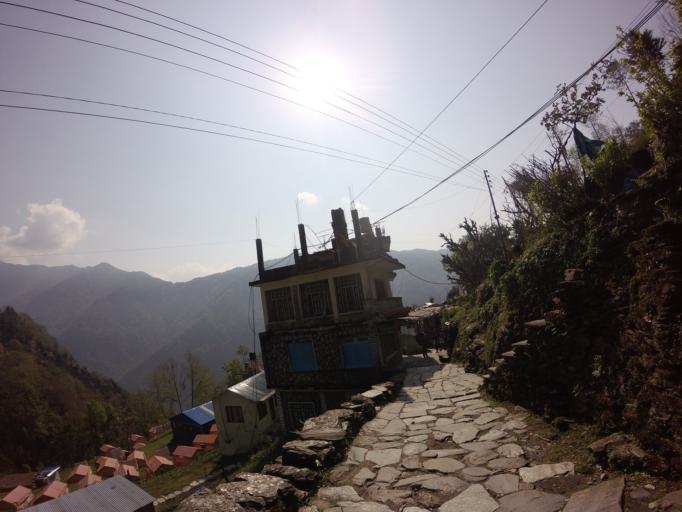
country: NP
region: Western Region
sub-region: Dhawalagiri Zone
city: Chitre
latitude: 28.3732
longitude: 83.8093
